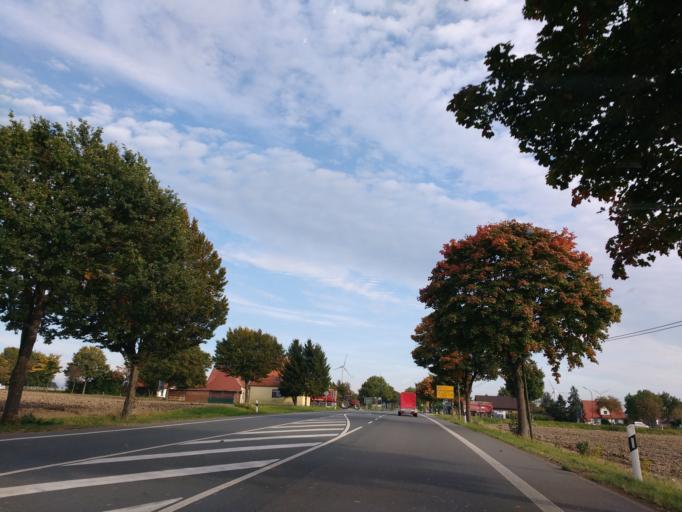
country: DE
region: North Rhine-Westphalia
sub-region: Regierungsbezirk Detmold
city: Paderborn
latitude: 51.6779
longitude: 8.8300
